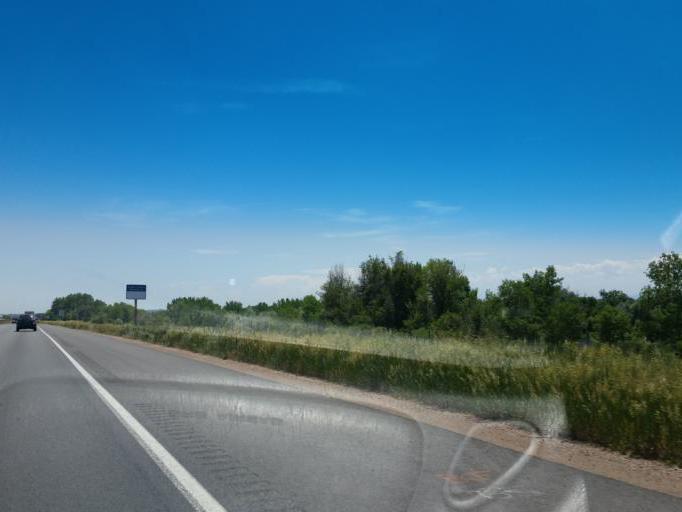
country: US
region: Colorado
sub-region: Larimer County
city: Fort Collins
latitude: 40.5478
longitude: -104.9985
